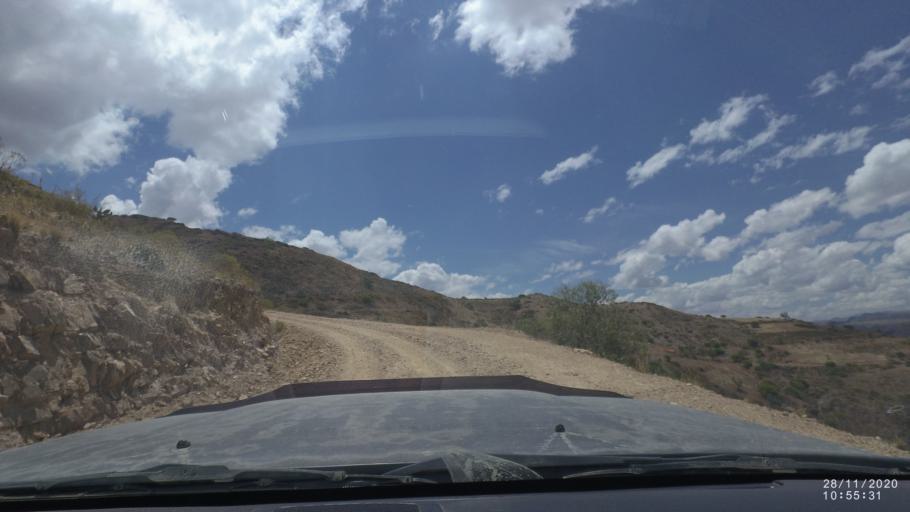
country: BO
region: Cochabamba
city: Capinota
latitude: -17.7764
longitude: -66.1146
